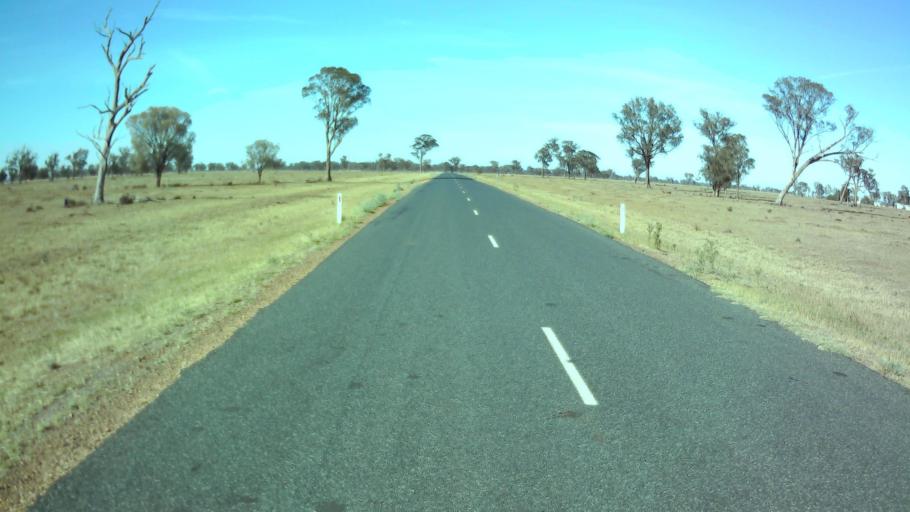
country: AU
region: New South Wales
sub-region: Weddin
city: Grenfell
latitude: -34.0460
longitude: 147.9243
